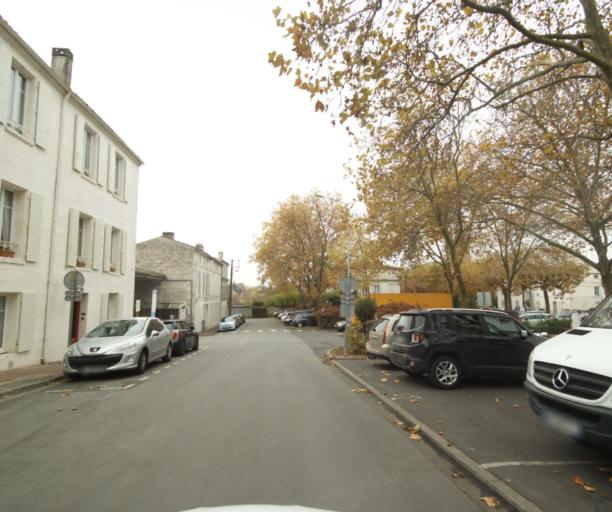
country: FR
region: Poitou-Charentes
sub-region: Departement de la Charente-Maritime
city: Saintes
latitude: 45.7452
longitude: -0.6380
